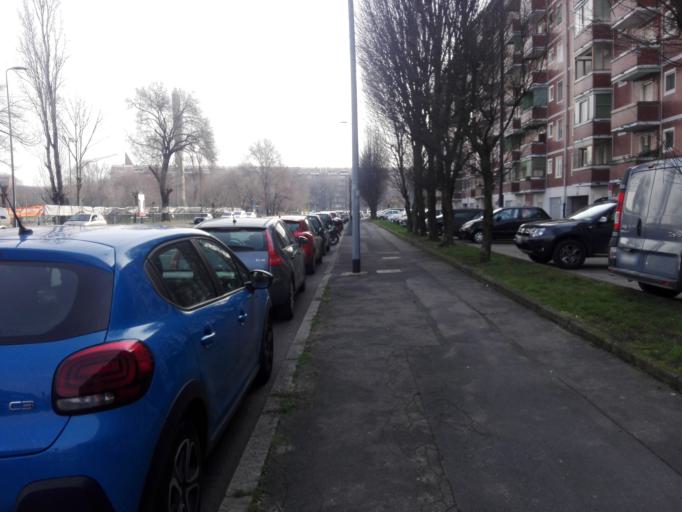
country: IT
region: Lombardy
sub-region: Citta metropolitana di Milano
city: Assago
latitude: 45.4310
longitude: 9.1571
